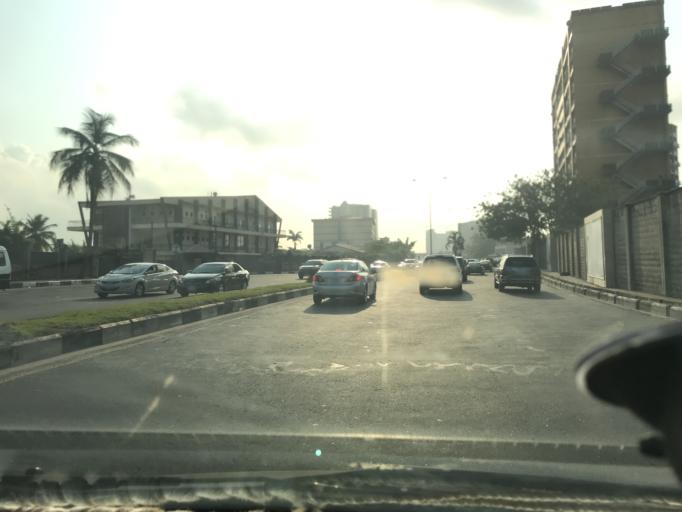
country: NG
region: Lagos
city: Ikoyi
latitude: 6.4402
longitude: 3.4352
